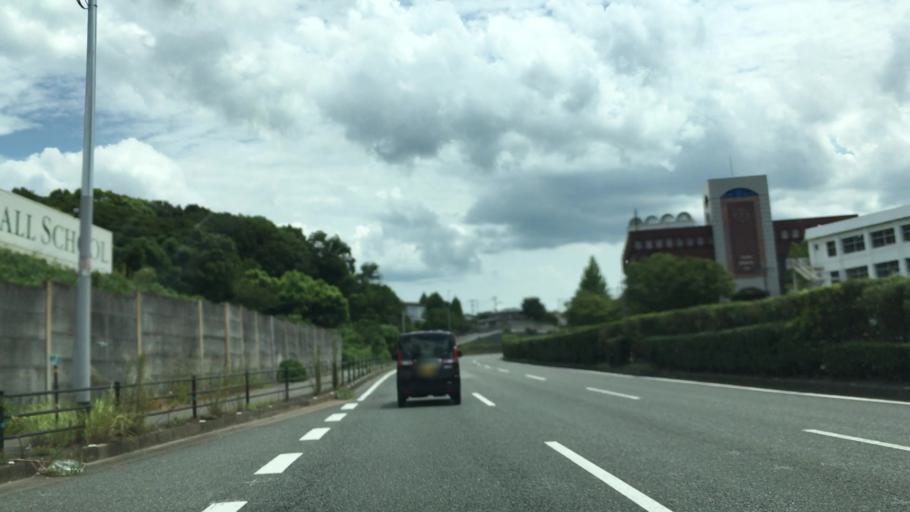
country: JP
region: Fukuoka
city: Dazaifu
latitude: 33.5070
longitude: 130.5268
